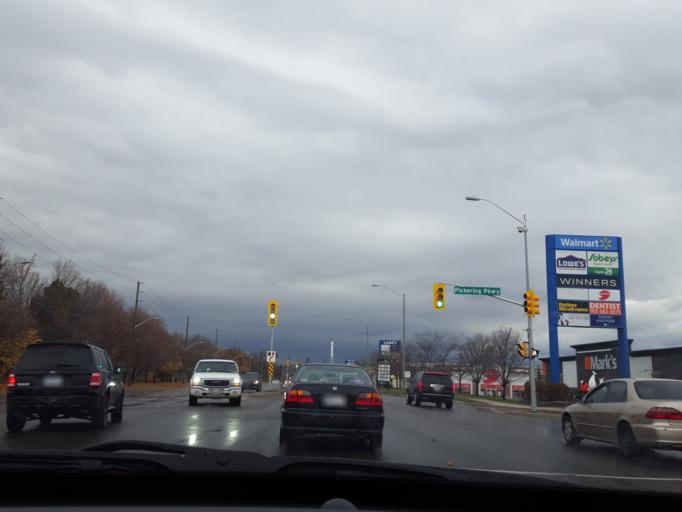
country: CA
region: Ontario
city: Ajax
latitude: 43.8435
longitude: -79.0722
